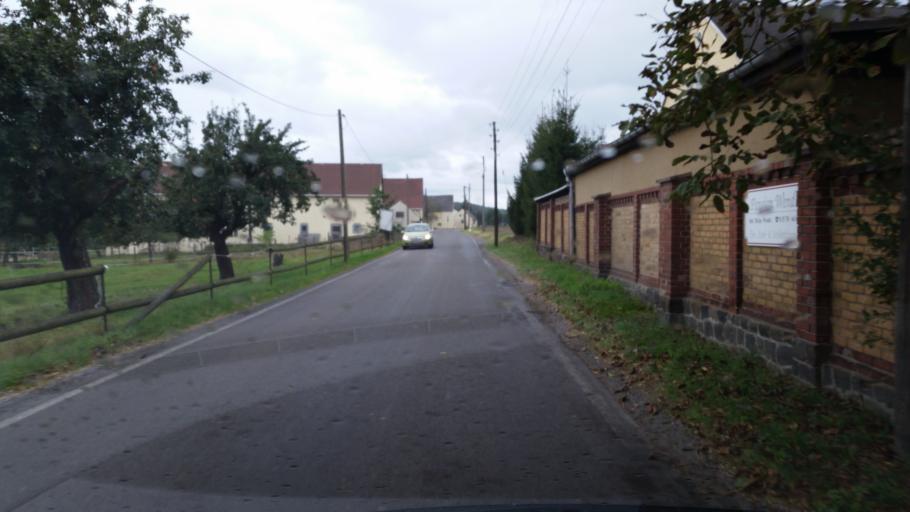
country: DE
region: Saxony
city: Kamenz
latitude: 51.2870
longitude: 14.0452
